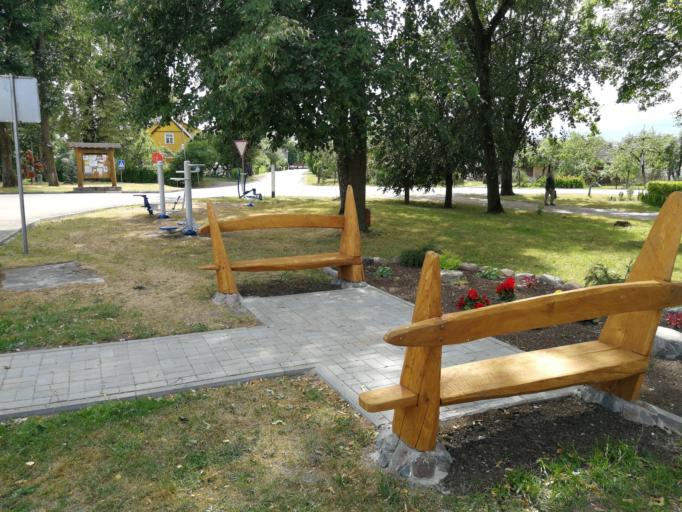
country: LT
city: Vilkija
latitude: 55.0838
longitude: 23.4173
